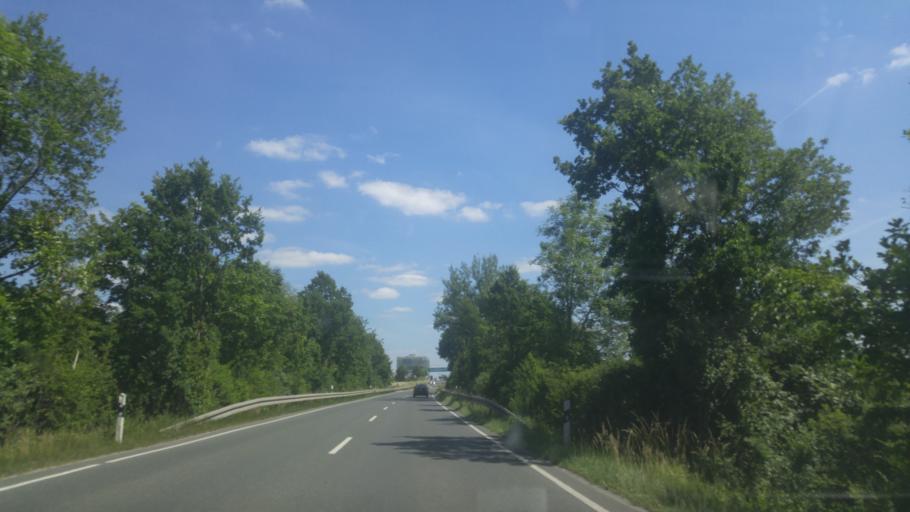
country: DE
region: Bavaria
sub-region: Regierungsbezirk Mittelfranken
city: Herzogenaurach
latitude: 49.5782
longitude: 10.8931
